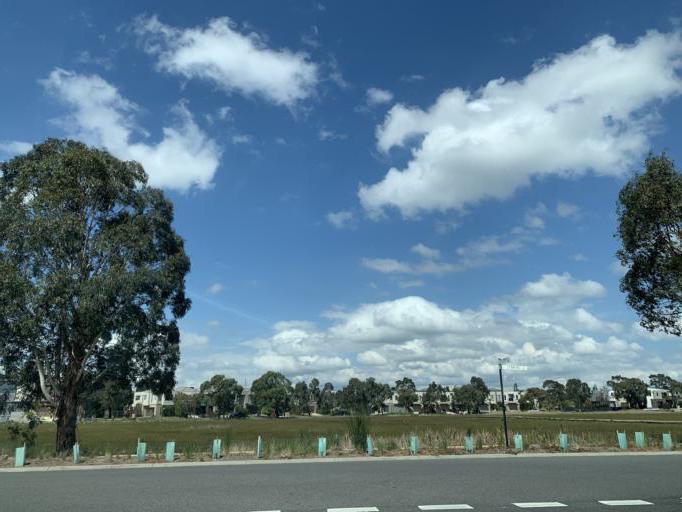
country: AU
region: Victoria
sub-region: Kingston
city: Mordialloc
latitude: -38.0049
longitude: 145.1017
